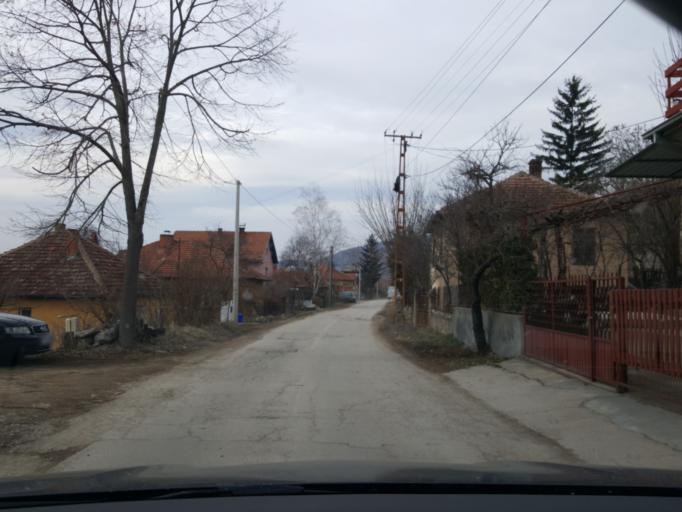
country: RS
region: Central Serbia
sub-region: Pirotski Okrug
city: Dimitrovgrad
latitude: 43.0037
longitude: 22.7619
